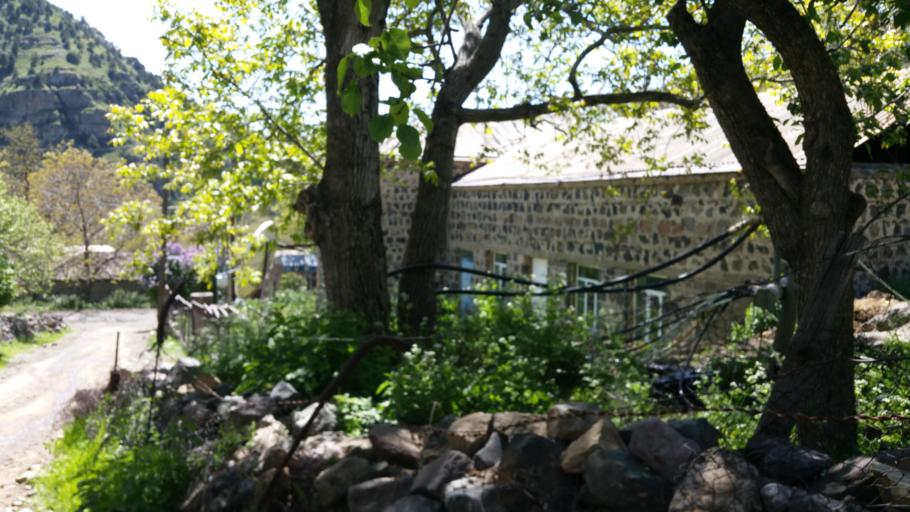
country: AM
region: Vayots' Dzori Marz
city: Yeghegis
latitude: 39.8720
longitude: 45.3594
